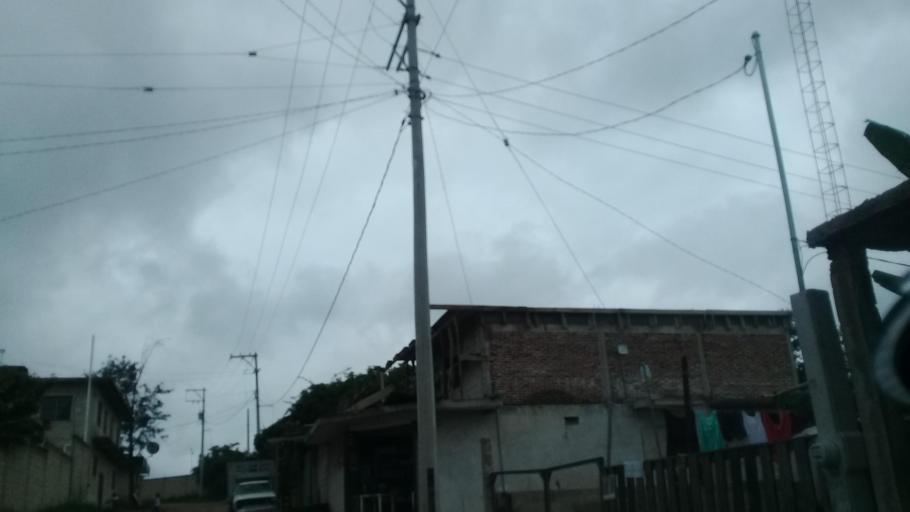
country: MX
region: Veracruz
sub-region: Emiliano Zapata
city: Las Trancas
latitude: 19.4975
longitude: -96.8651
